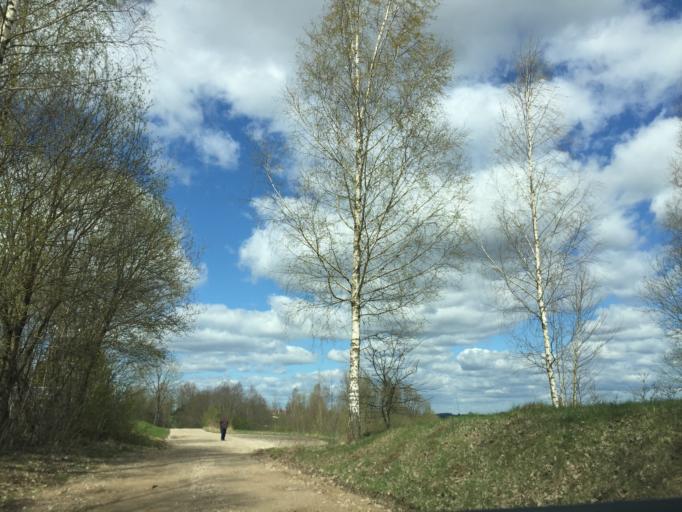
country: LV
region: Rezekne
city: Rezekne
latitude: 56.4858
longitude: 27.3330
